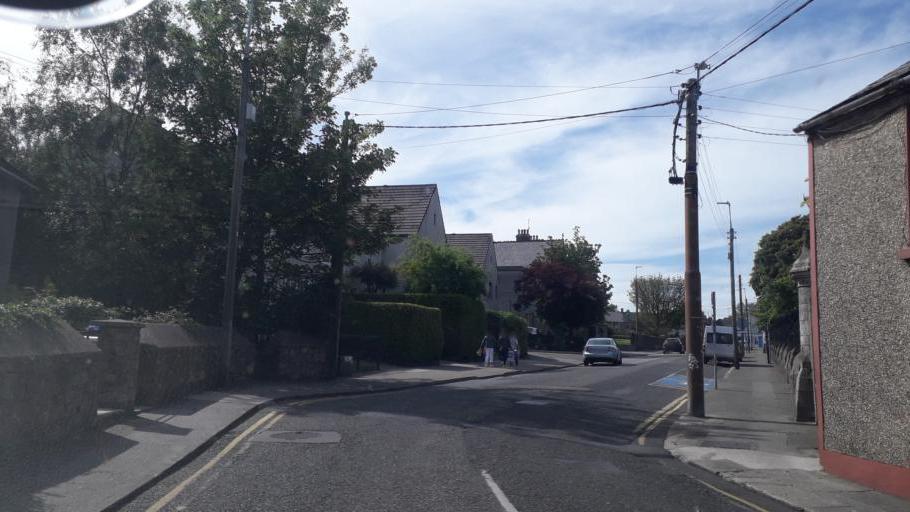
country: IE
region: Leinster
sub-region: Loch Garman
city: Loch Garman
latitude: 52.3332
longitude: -6.4612
